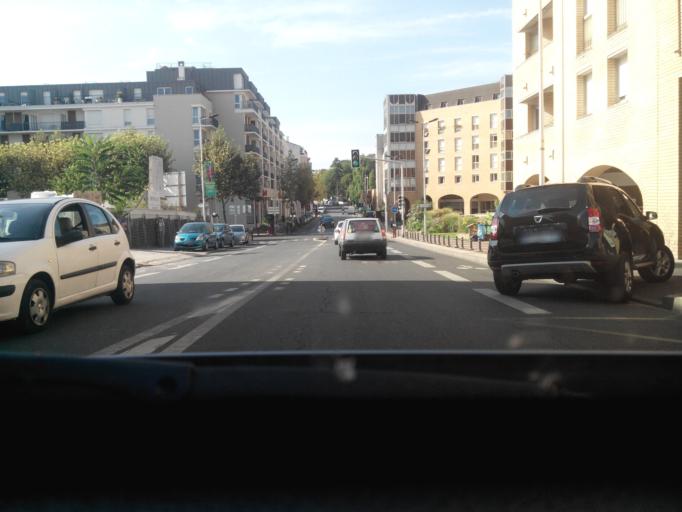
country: FR
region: Ile-de-France
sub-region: Departement du Val-de-Marne
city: Cachan
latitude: 48.7928
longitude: 2.3364
